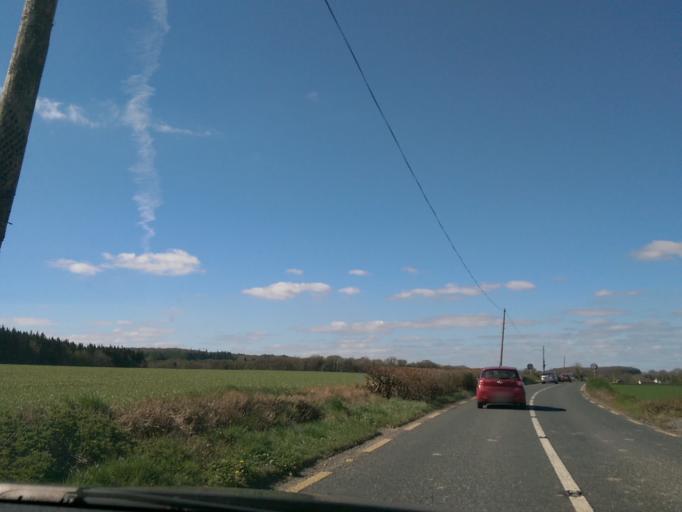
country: IE
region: Leinster
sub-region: Laois
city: Stradbally
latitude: 53.0075
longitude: -7.0796
